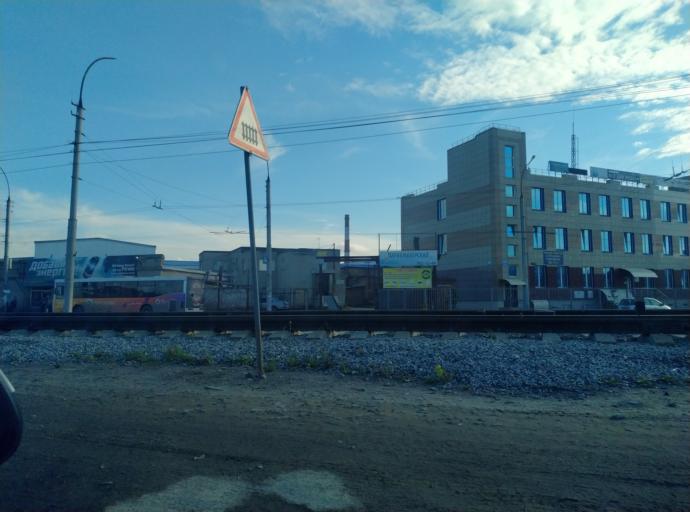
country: RU
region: Novosibirsk
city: Tolmachevo
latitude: 55.0138
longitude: 82.8088
